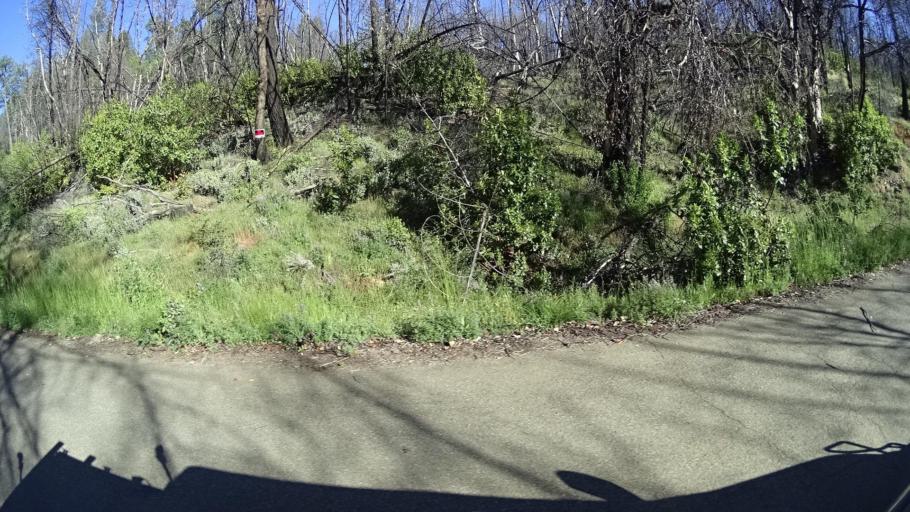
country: US
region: California
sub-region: Lake County
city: Upper Lake
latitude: 39.3959
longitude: -122.9693
